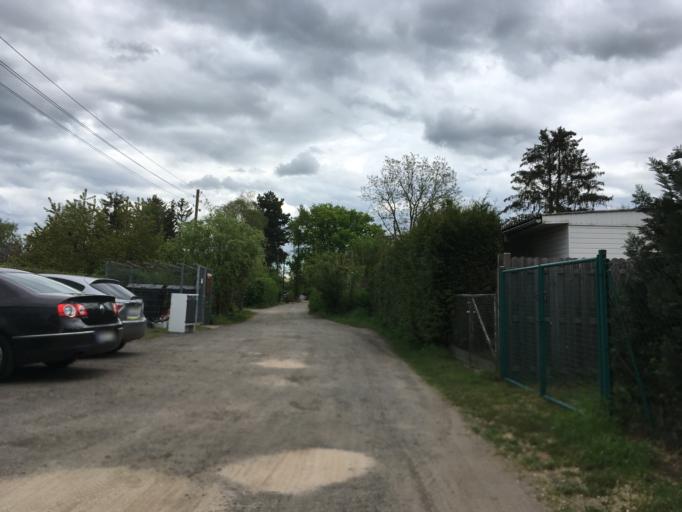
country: DE
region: Berlin
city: Blankenfelde
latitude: 52.6192
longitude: 13.4124
